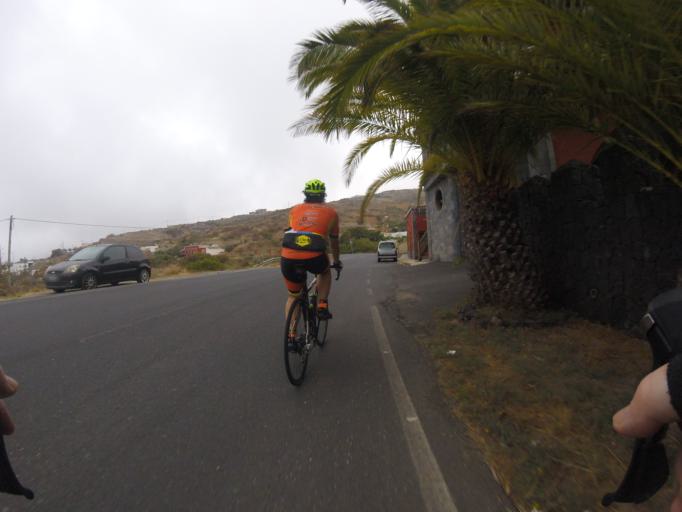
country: ES
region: Canary Islands
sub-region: Provincia de Santa Cruz de Tenerife
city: Guimar
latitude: 28.2870
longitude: -16.4049
